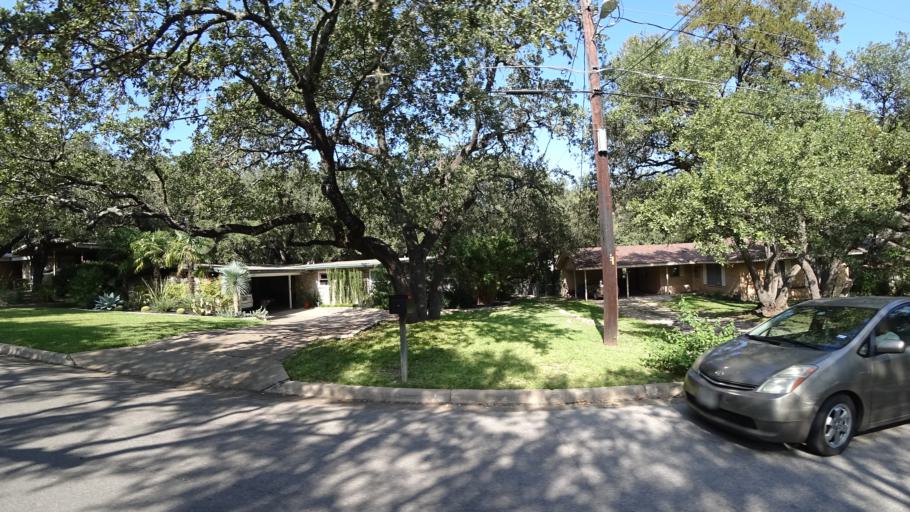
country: US
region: Texas
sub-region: Travis County
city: West Lake Hills
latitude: 30.2855
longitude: -97.8078
